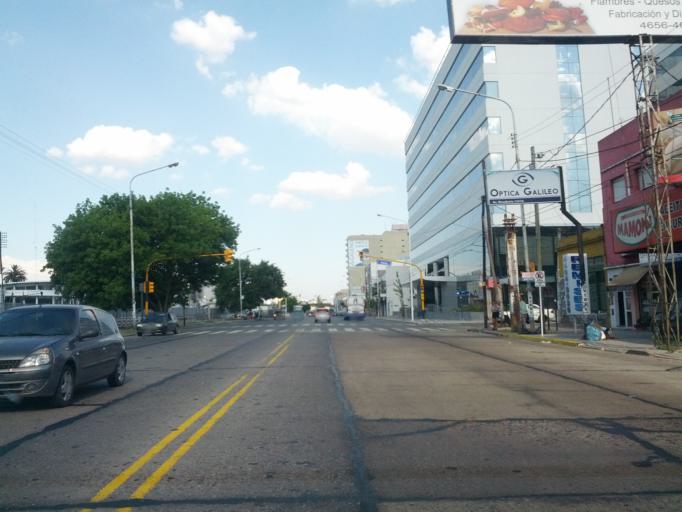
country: AR
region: Buenos Aires
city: San Justo
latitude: -34.6399
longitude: -58.5548
